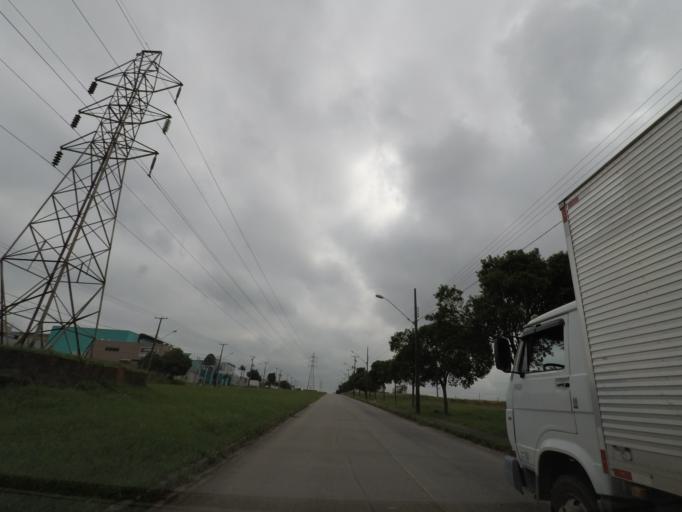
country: BR
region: Parana
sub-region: Curitiba
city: Curitiba
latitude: -25.5089
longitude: -49.3116
